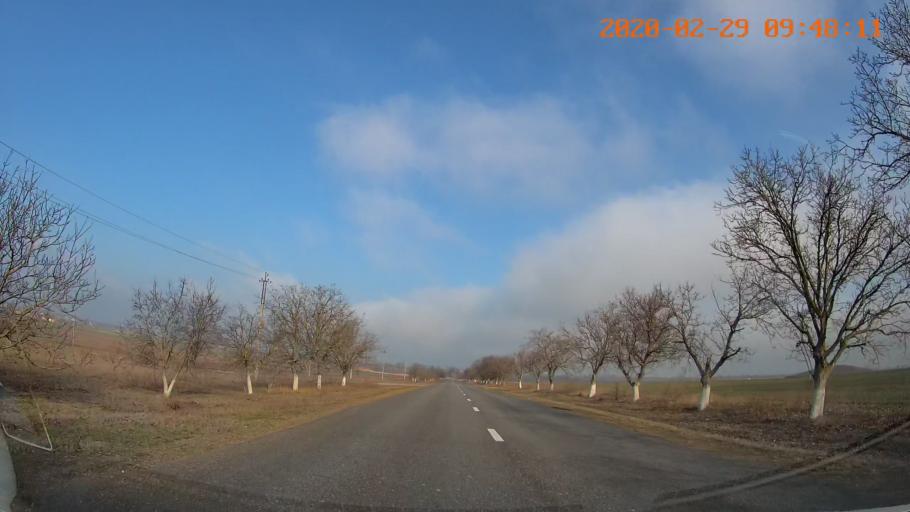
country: MD
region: Telenesti
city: Crasnoe
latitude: 46.6851
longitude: 29.7861
